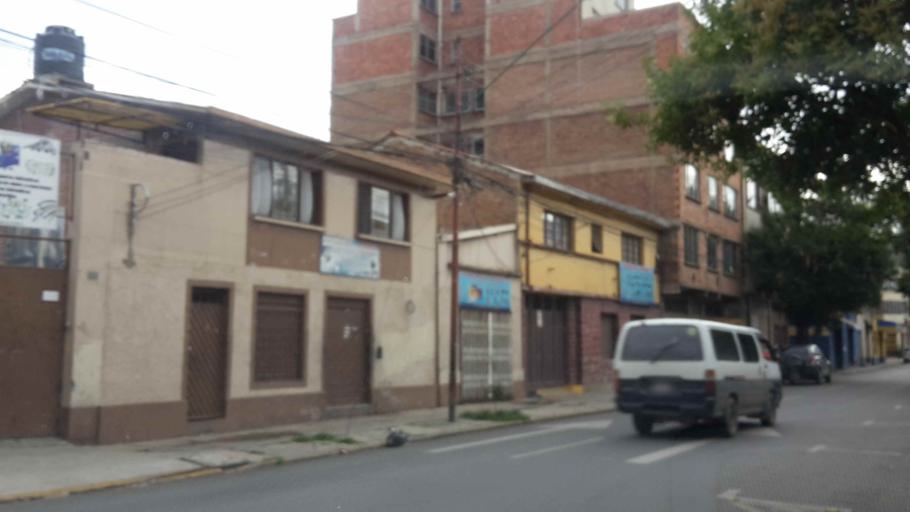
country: BO
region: Cochabamba
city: Cochabamba
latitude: -17.3983
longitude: -66.1611
